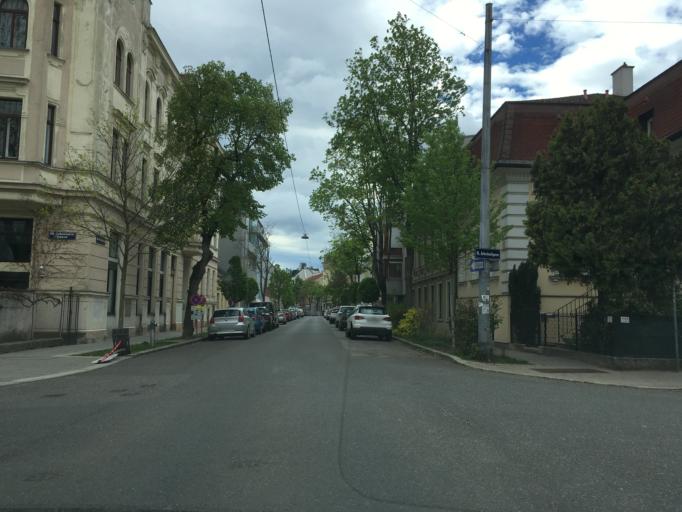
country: AT
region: Vienna
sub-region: Wien Stadt
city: Vienna
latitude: 48.2443
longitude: 16.3408
